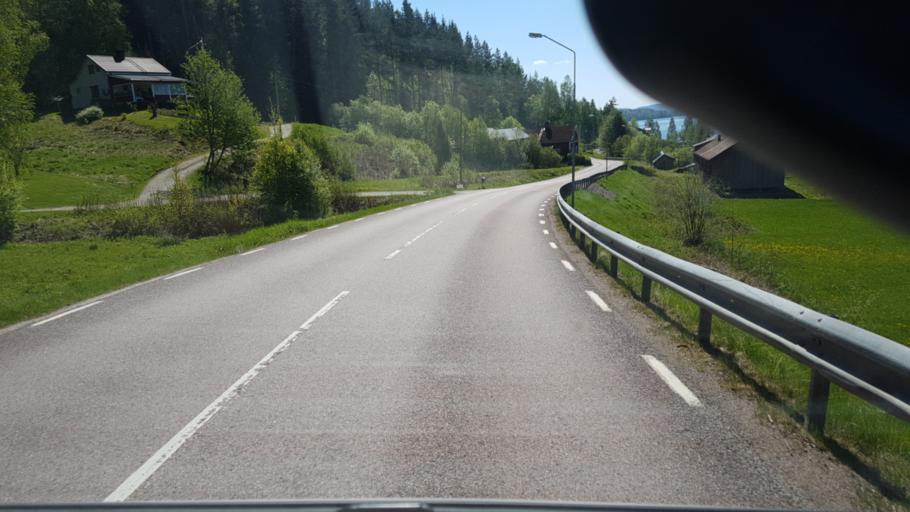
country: SE
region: Vaermland
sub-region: Arvika Kommun
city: Arvika
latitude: 59.8478
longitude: 12.5498
